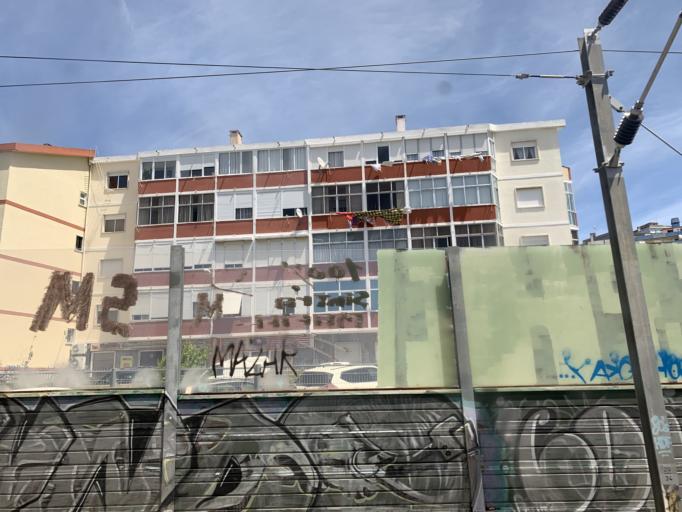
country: PT
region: Lisbon
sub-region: Sintra
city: Rio de Mouro
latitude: 38.7849
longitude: -9.3229
